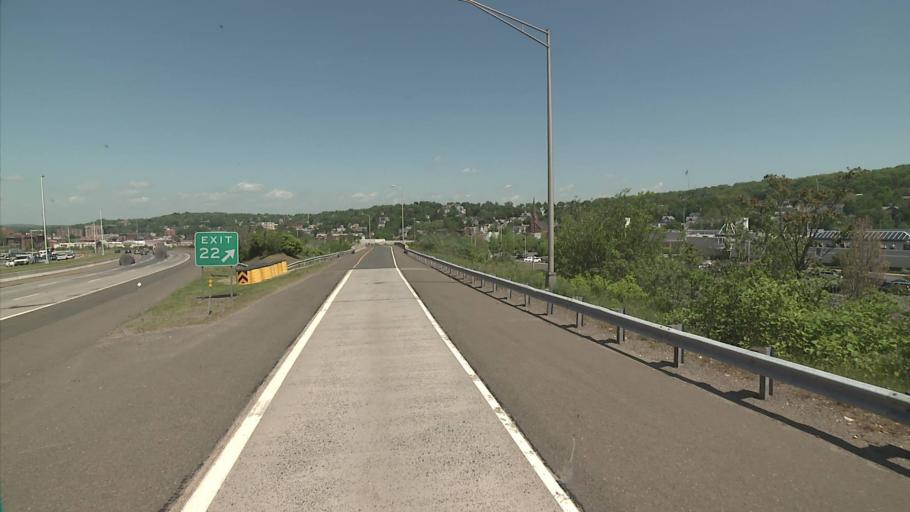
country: US
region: Connecticut
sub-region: New Haven County
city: Waterbury
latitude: 41.5491
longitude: -73.0277
